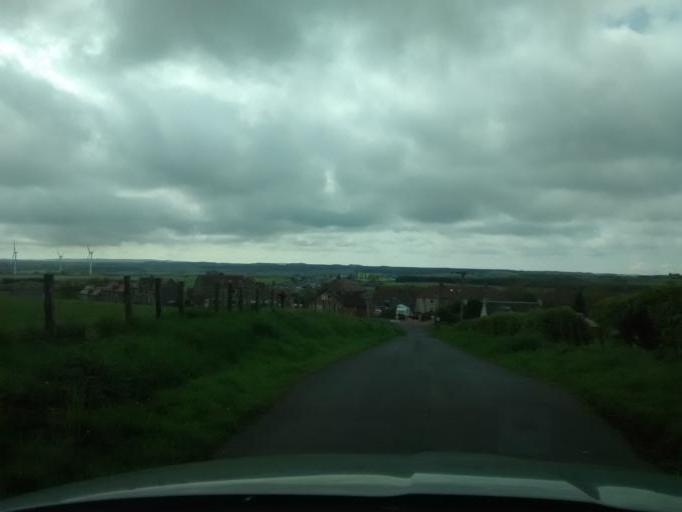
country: GB
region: Scotland
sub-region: North Lanarkshire
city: Harthill
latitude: 55.8870
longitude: -3.7659
